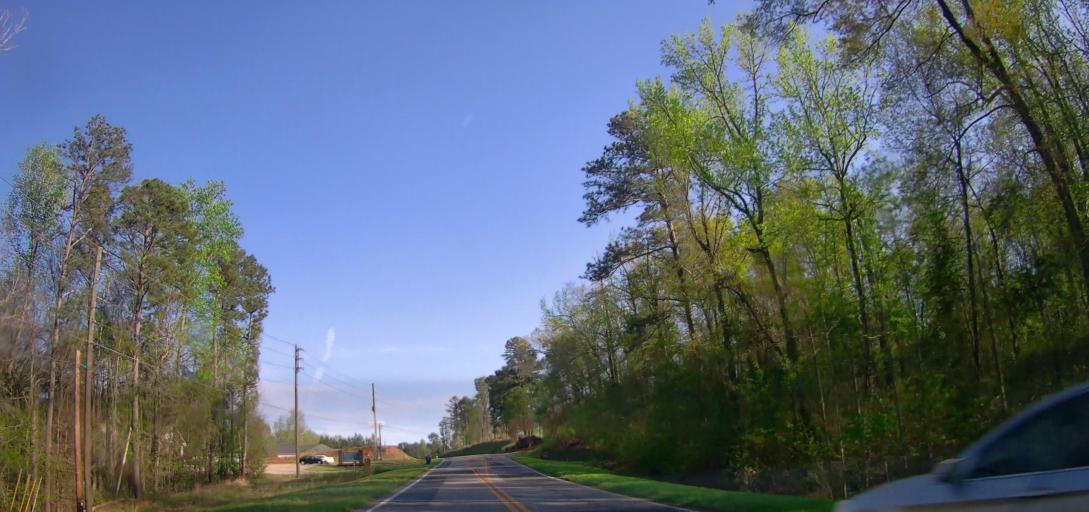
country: US
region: Georgia
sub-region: Baldwin County
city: Milledgeville
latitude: 33.1512
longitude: -83.2600
